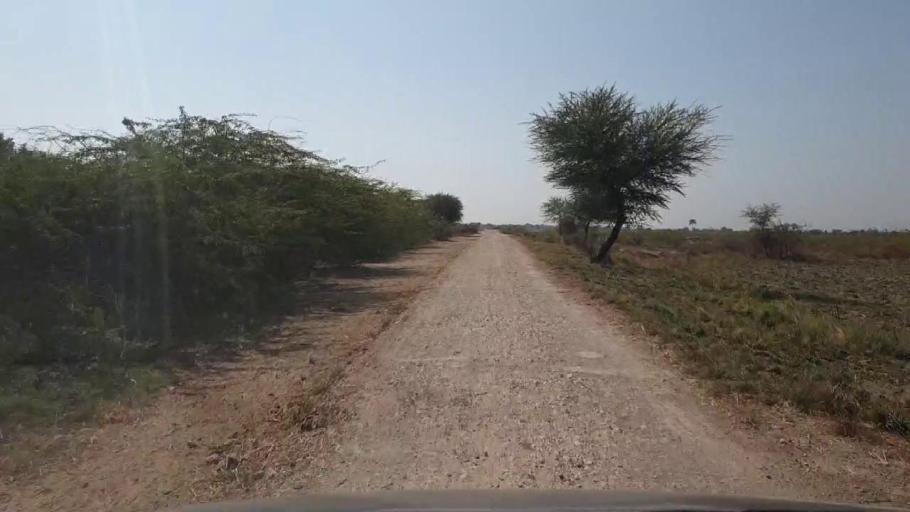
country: PK
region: Sindh
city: Samaro
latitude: 25.2349
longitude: 69.2824
